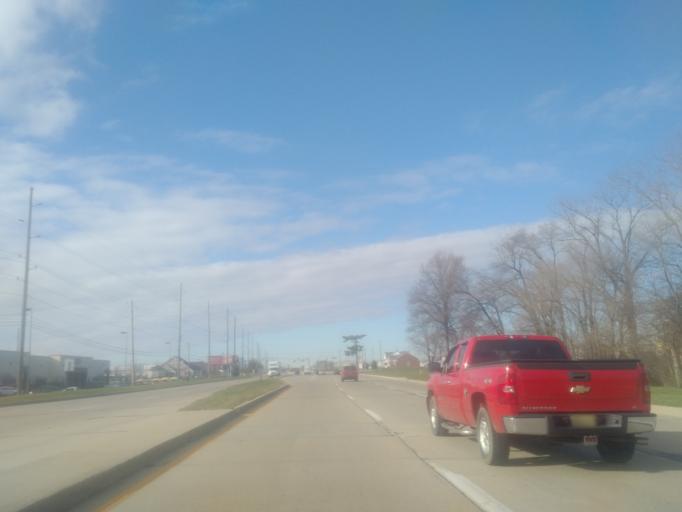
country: US
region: Indiana
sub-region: Boone County
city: Zionsville
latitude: 39.9116
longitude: -86.2380
